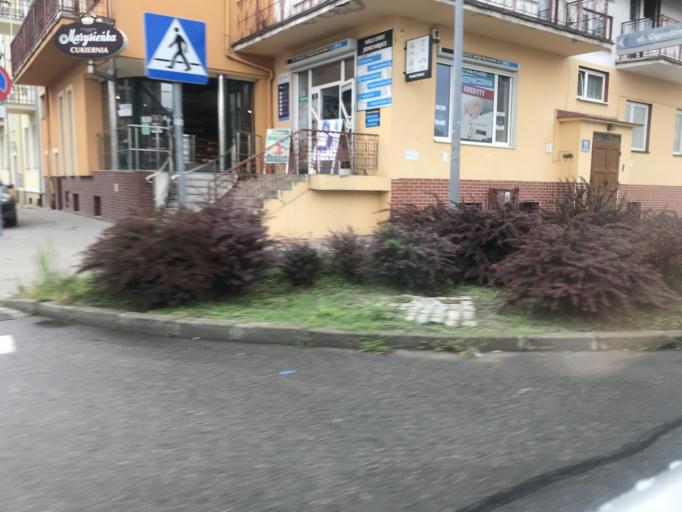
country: PL
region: Warmian-Masurian Voivodeship
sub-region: Powiat elblaski
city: Elblag
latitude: 54.1545
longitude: 19.4196
